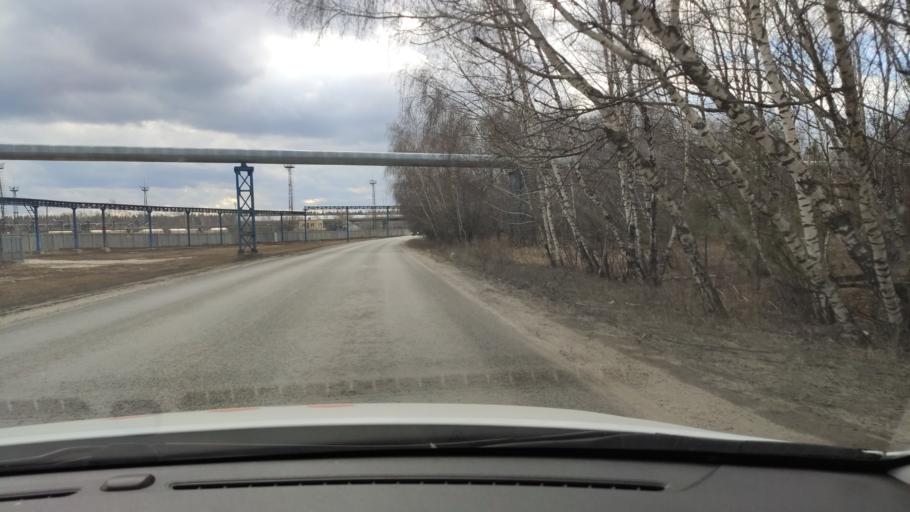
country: RU
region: Tatarstan
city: Staroye Arakchino
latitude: 55.8650
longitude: 48.9716
